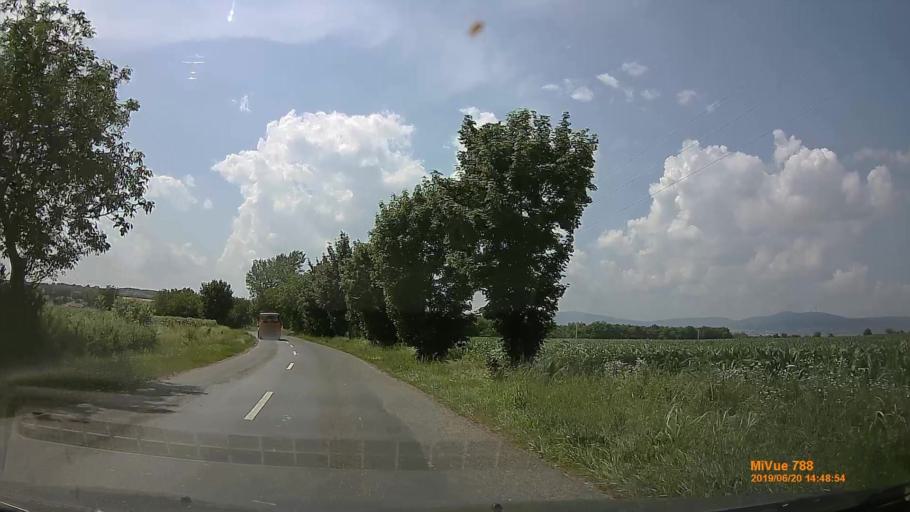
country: HU
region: Baranya
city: Kozarmisleny
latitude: 46.0163
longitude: 18.2819
